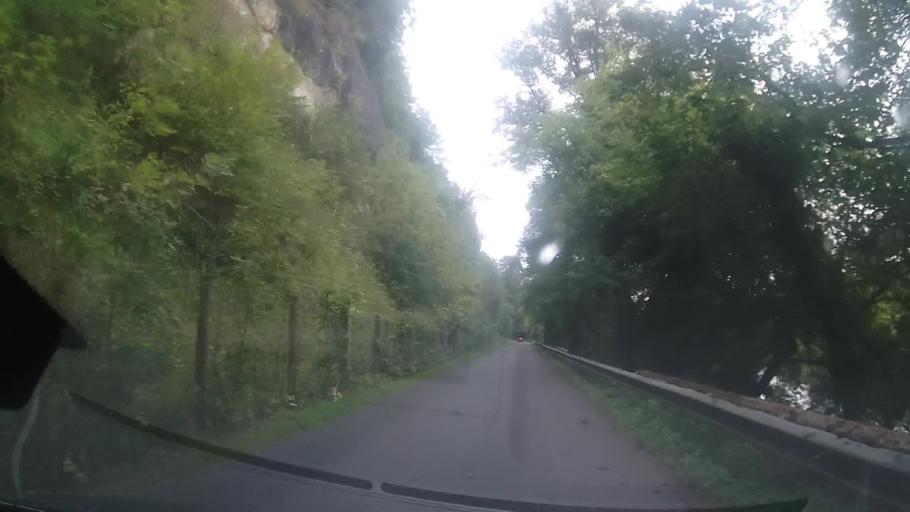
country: FR
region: Aquitaine
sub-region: Departement de la Dordogne
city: Domme
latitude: 44.8057
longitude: 1.2162
